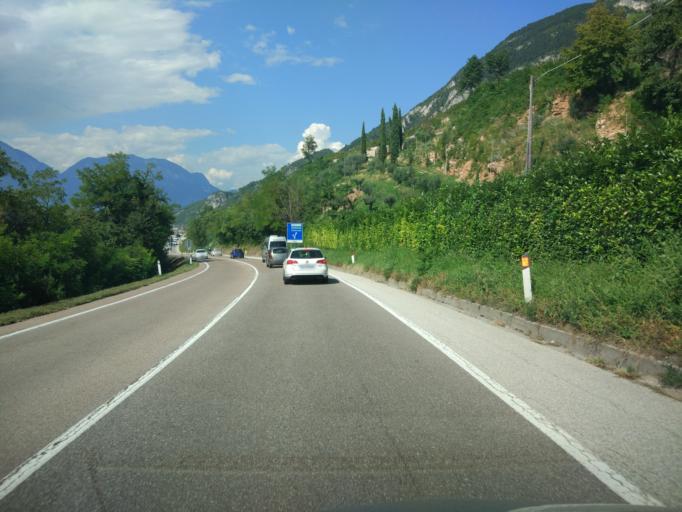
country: IT
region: Trentino-Alto Adige
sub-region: Provincia di Trento
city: Trento
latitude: 46.0871
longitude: 11.1251
